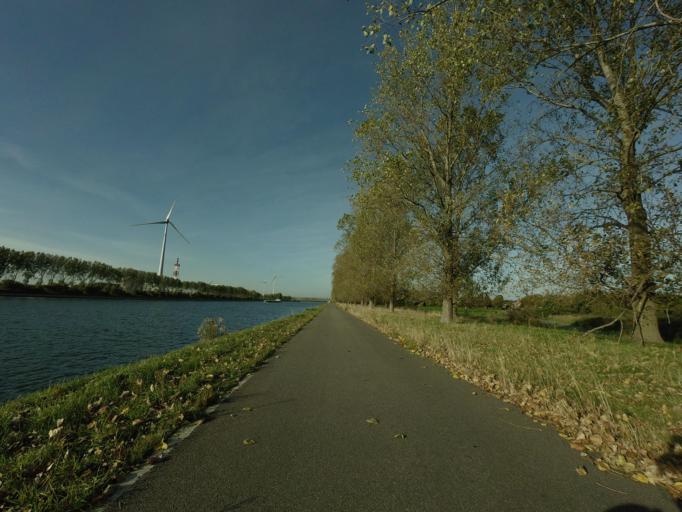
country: NL
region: North Brabant
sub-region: Gemeente Woensdrecht
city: Woensdrecht
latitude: 51.3567
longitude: 4.3019
